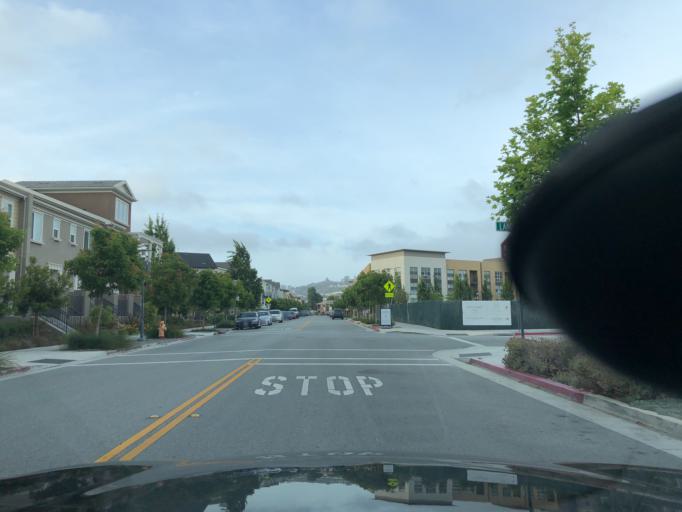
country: US
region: California
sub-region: San Mateo County
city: Foster City
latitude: 37.5427
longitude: -122.2967
